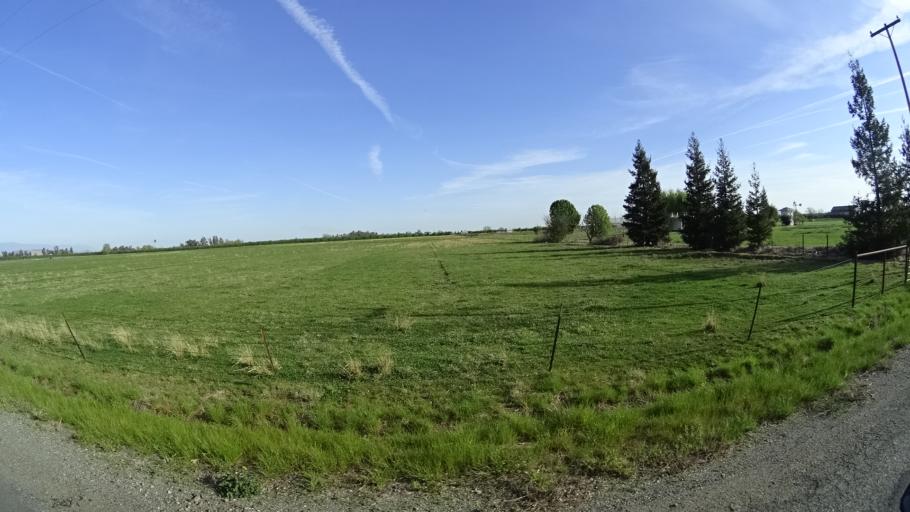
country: US
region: California
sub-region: Glenn County
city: Orland
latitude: 39.7188
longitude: -122.2396
